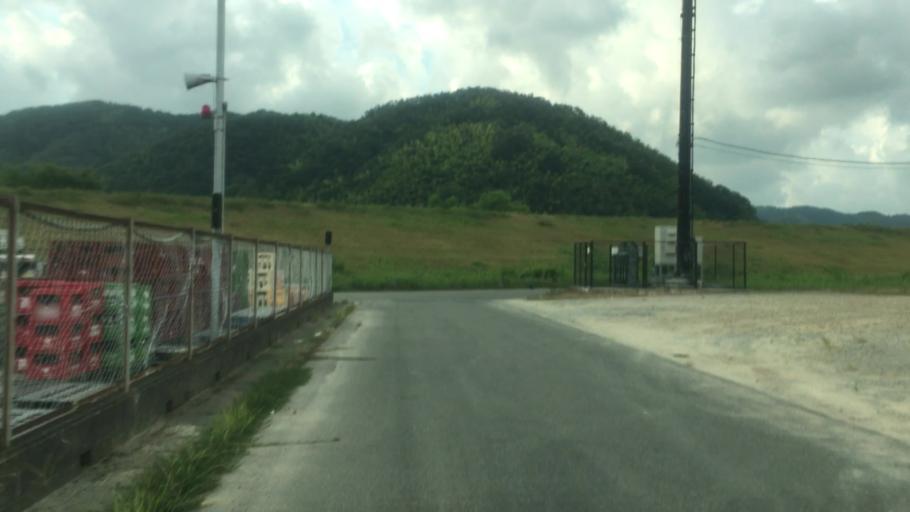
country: JP
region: Hyogo
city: Toyooka
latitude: 35.5626
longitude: 134.8026
